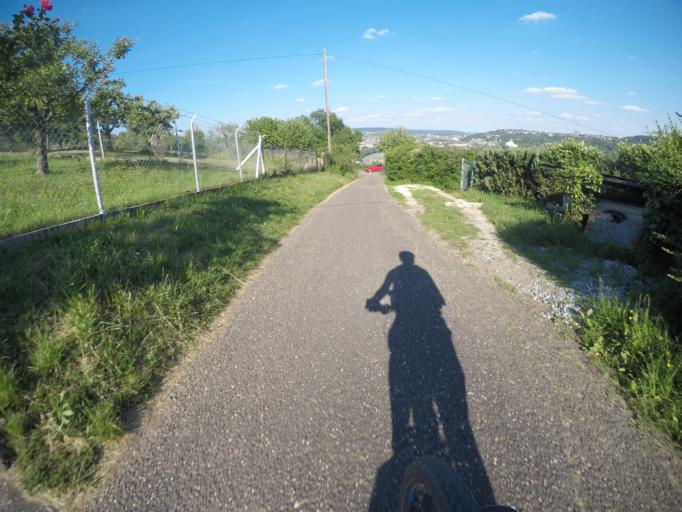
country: DE
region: Baden-Wuerttemberg
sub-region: Regierungsbezirk Stuttgart
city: Ostfildern
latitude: 48.7396
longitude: 9.2654
